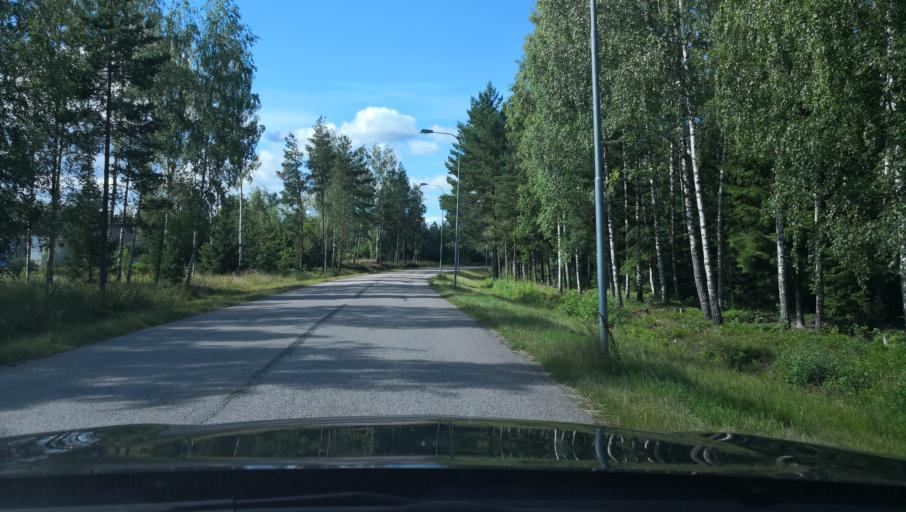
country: SE
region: Vaestmanland
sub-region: Surahammars Kommun
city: Surahammar
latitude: 59.6954
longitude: 16.2431
